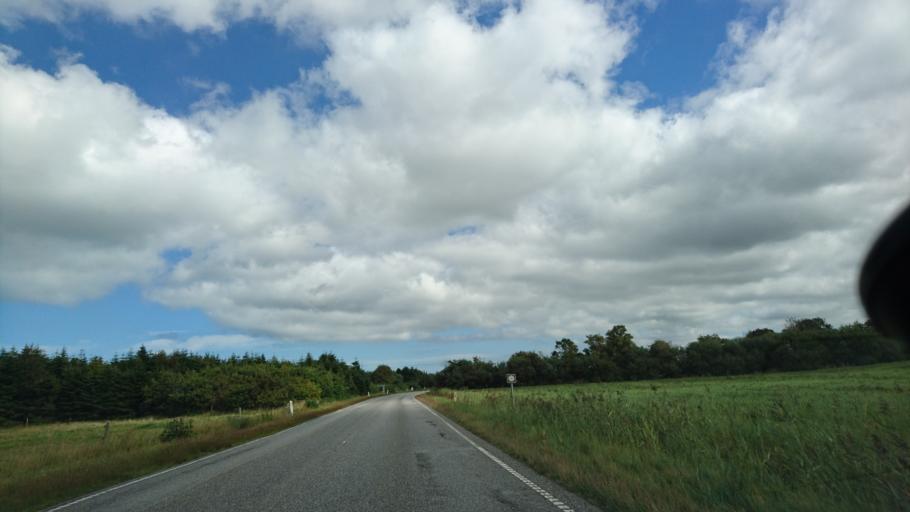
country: DK
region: North Denmark
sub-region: Hjorring Kommune
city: Sindal
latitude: 57.5706
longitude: 10.1188
